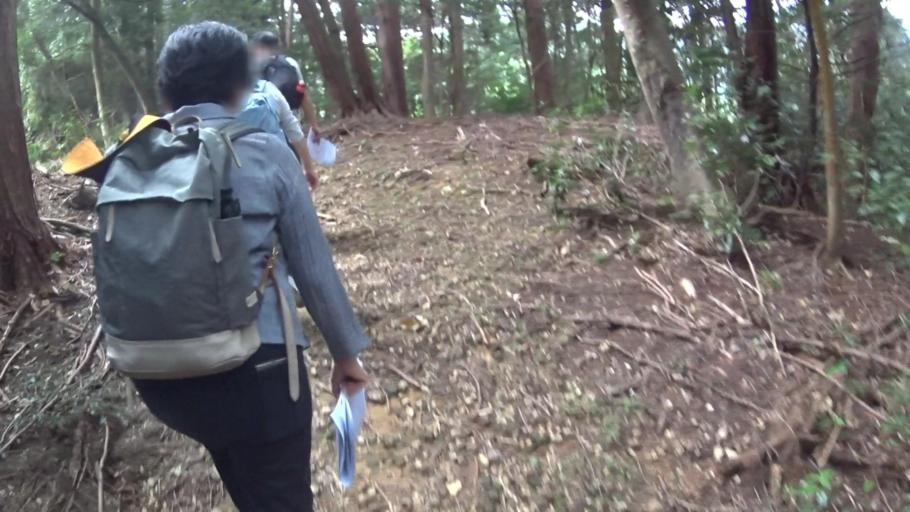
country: JP
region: Osaka
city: Kishiwada
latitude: 34.4988
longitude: 135.3314
